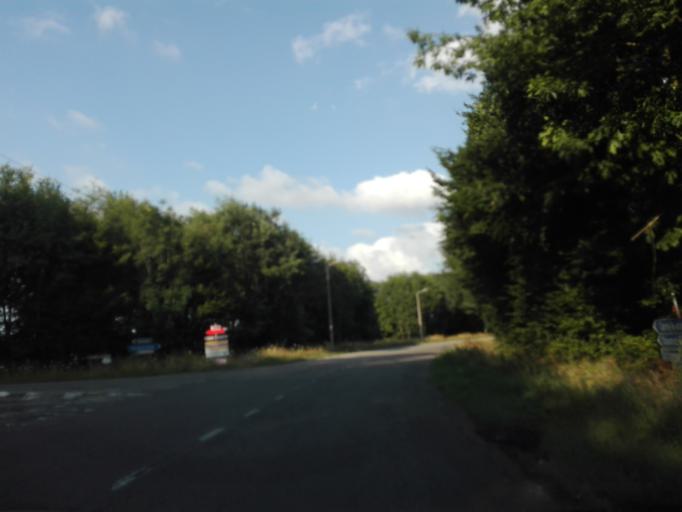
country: BE
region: Wallonia
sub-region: Province du Brabant Wallon
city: Louvain-la-Neuve
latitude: 50.6661
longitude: 4.6565
